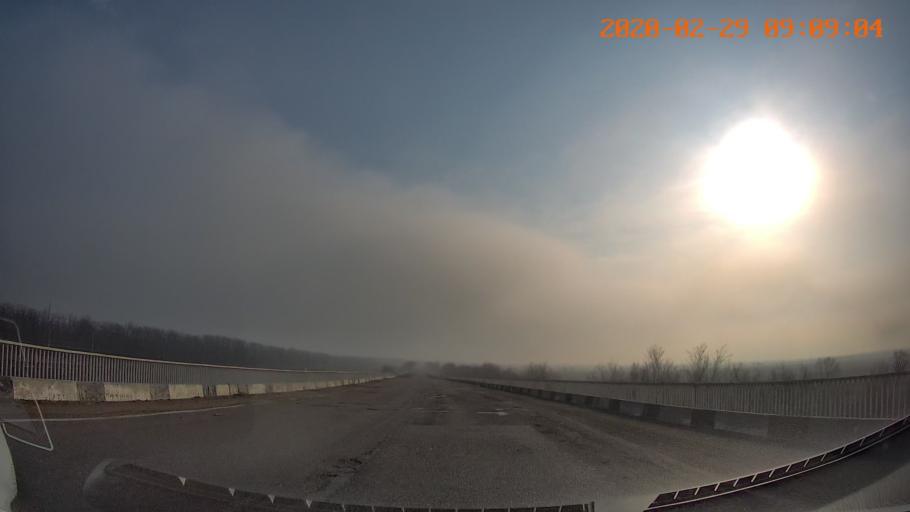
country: MD
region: Telenesti
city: Slobozia
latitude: 46.8450
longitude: 29.7568
